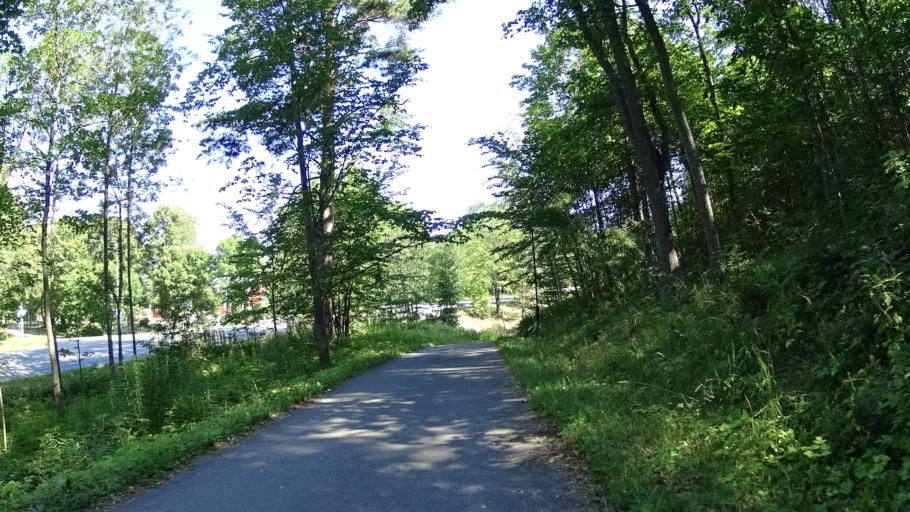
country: FI
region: Haeme
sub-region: Haemeenlinna
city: Haemeenlinna
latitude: 61.0259
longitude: 24.4457
